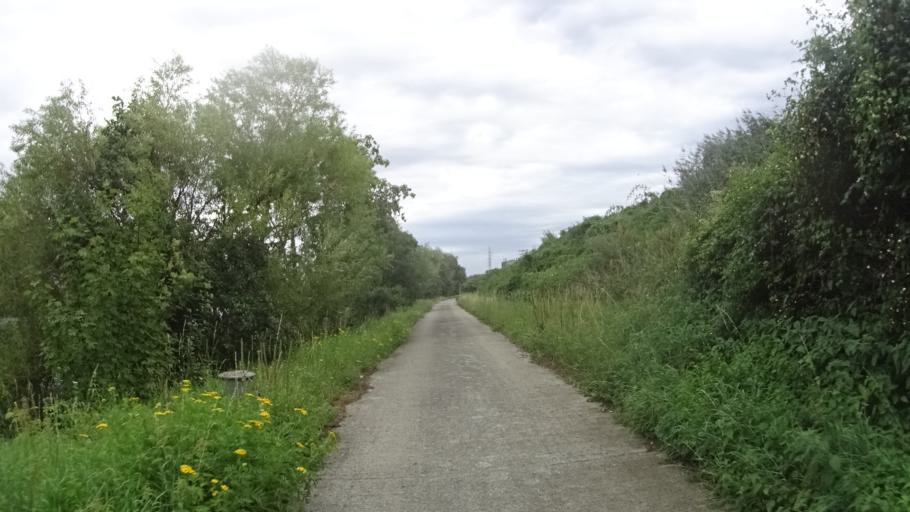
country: BE
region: Wallonia
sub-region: Province de Liege
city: Engis
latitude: 50.5682
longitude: 5.3745
